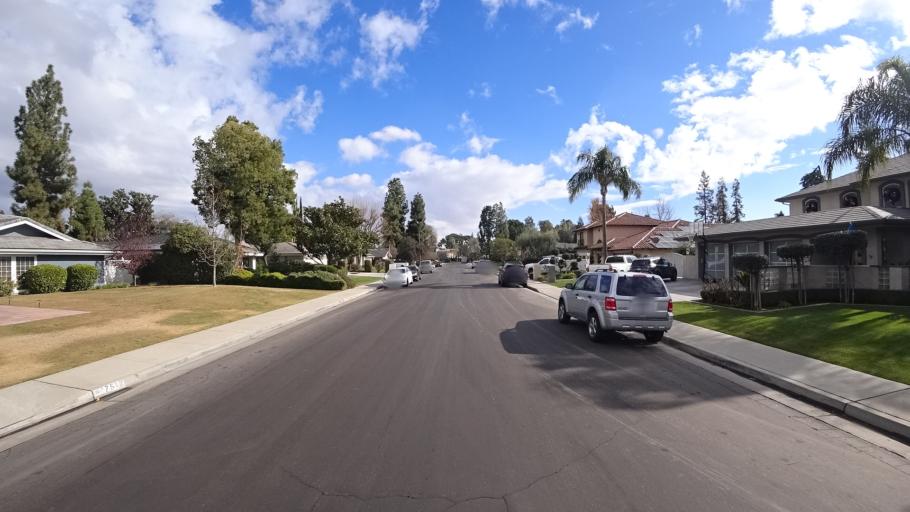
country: US
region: California
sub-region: Kern County
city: Greenacres
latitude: 35.3462
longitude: -119.0870
